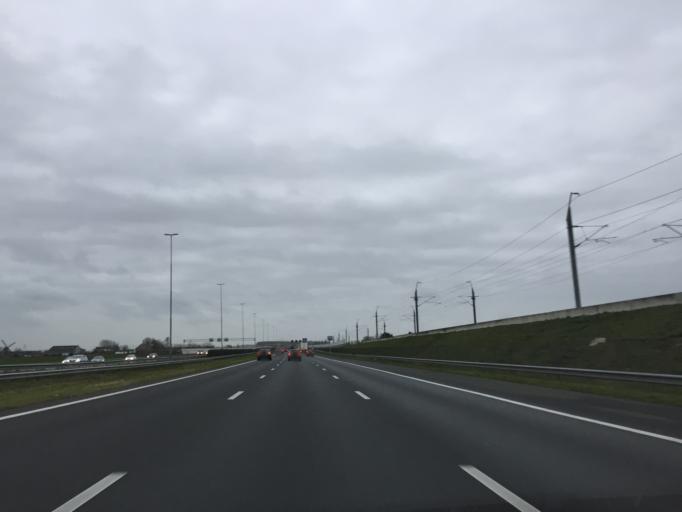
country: NL
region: South Holland
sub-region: Gemeente Leiderdorp
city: Leiderdorp
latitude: 52.1798
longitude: 4.5880
